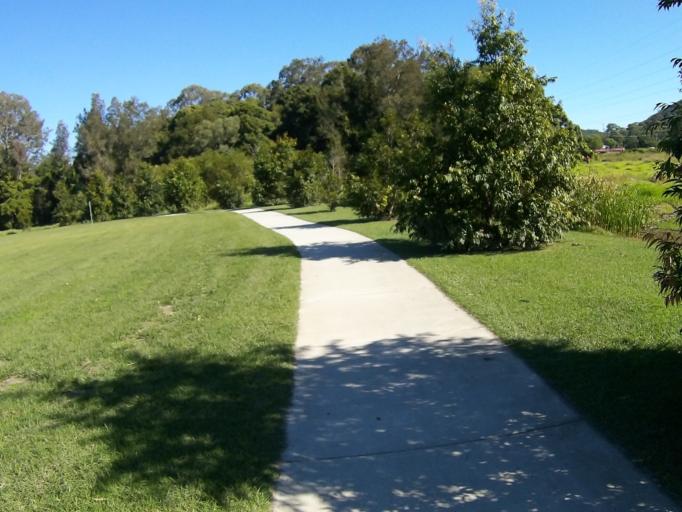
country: AU
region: Queensland
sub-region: Logan
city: Windaroo
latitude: -27.7356
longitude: 153.1982
